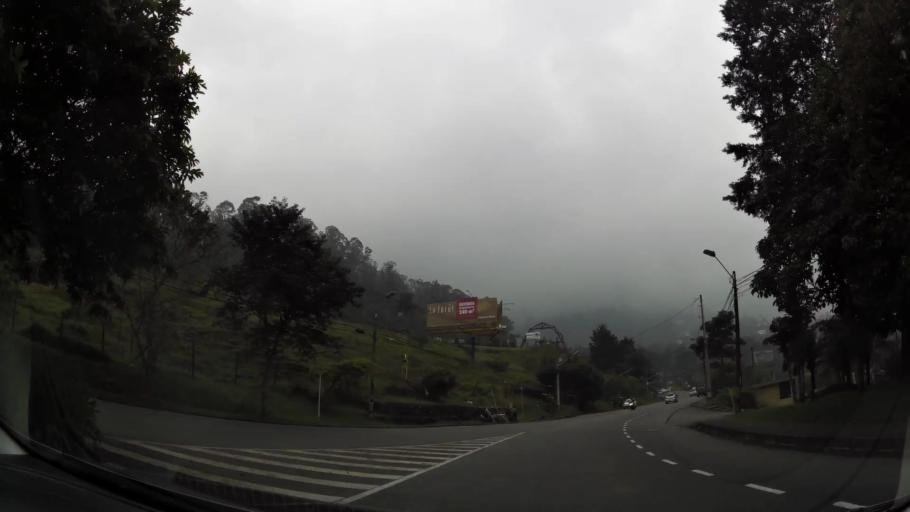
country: CO
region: Antioquia
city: Envigado
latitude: 6.1849
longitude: -75.5523
